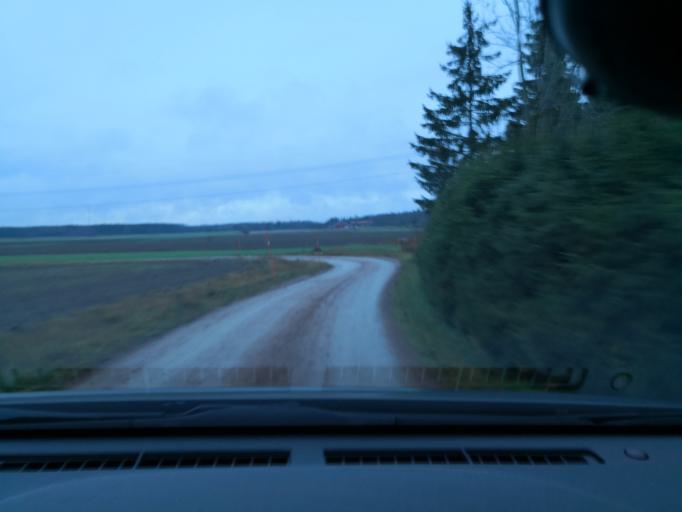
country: SE
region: Vaestmanland
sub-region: Hallstahammars Kommun
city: Kolback
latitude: 59.5635
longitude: 16.1807
